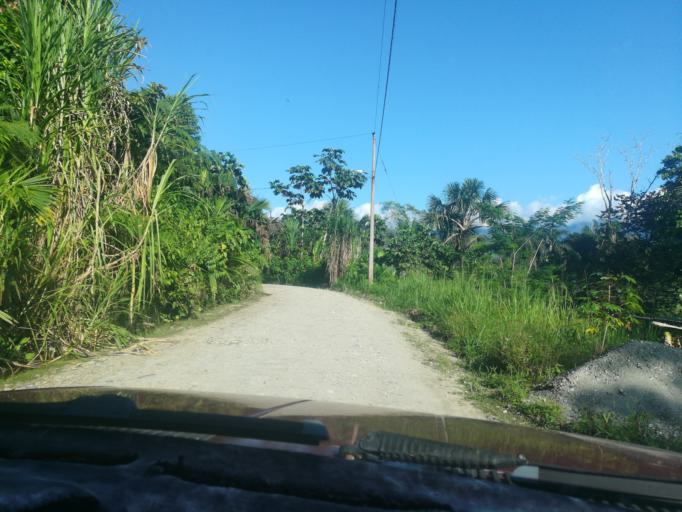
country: EC
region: Napo
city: Tena
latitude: -0.9917
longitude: -77.8290
